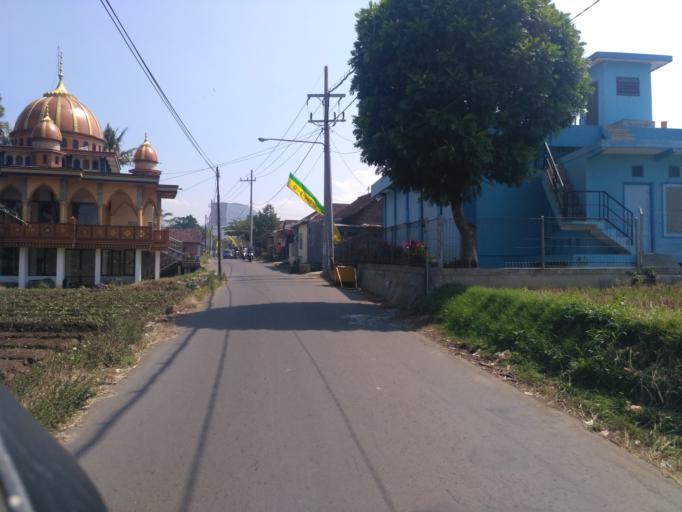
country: ID
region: East Java
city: Batu
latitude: -7.9054
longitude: 112.5832
